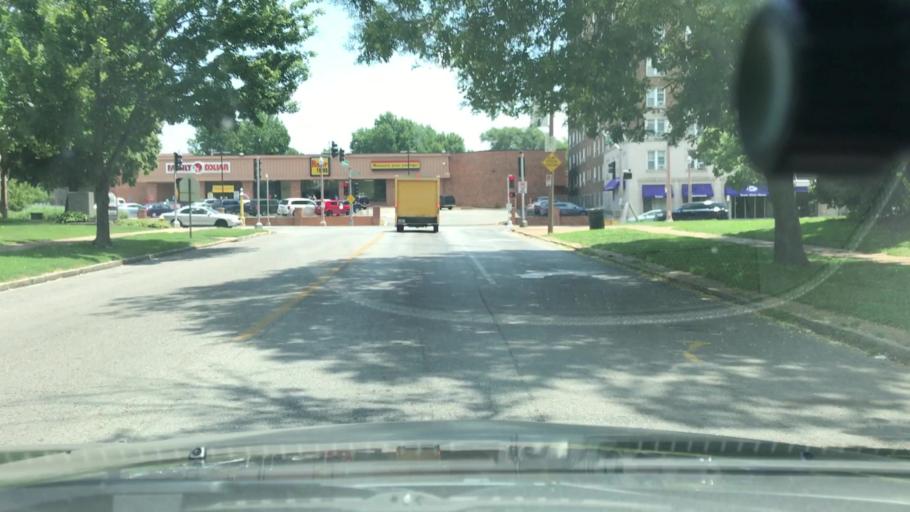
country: US
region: Missouri
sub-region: City of Saint Louis
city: St. Louis
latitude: 38.6073
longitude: -90.2421
